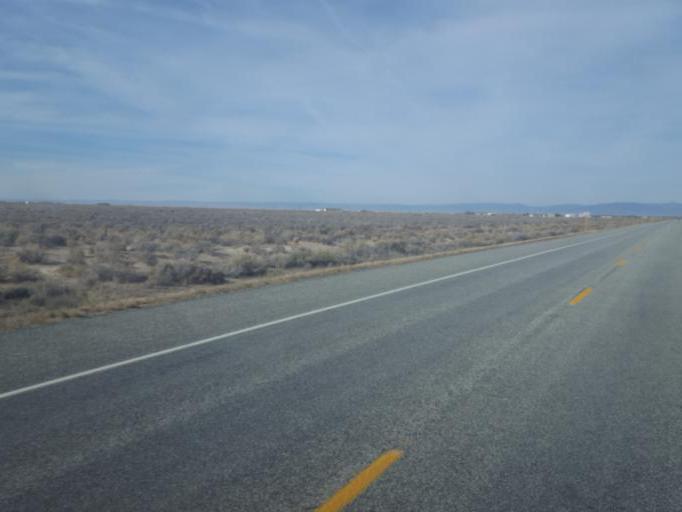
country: US
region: Colorado
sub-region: Alamosa County
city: Alamosa East
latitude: 37.4747
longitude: -105.6765
